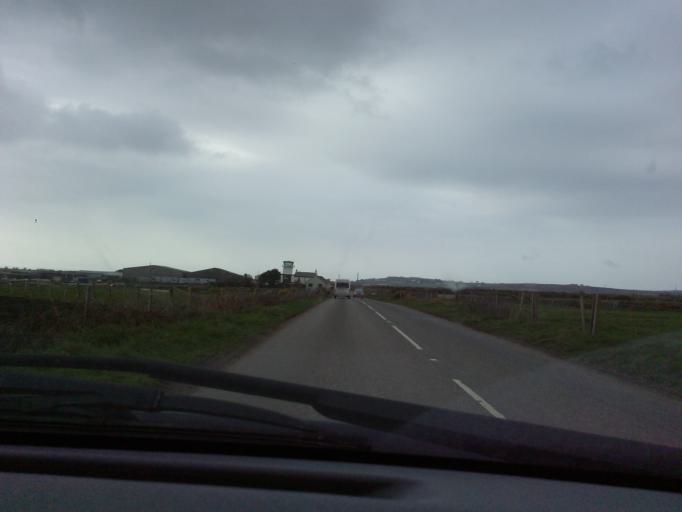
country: GB
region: England
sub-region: Cornwall
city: Saint Just
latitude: 50.0996
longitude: -5.6650
